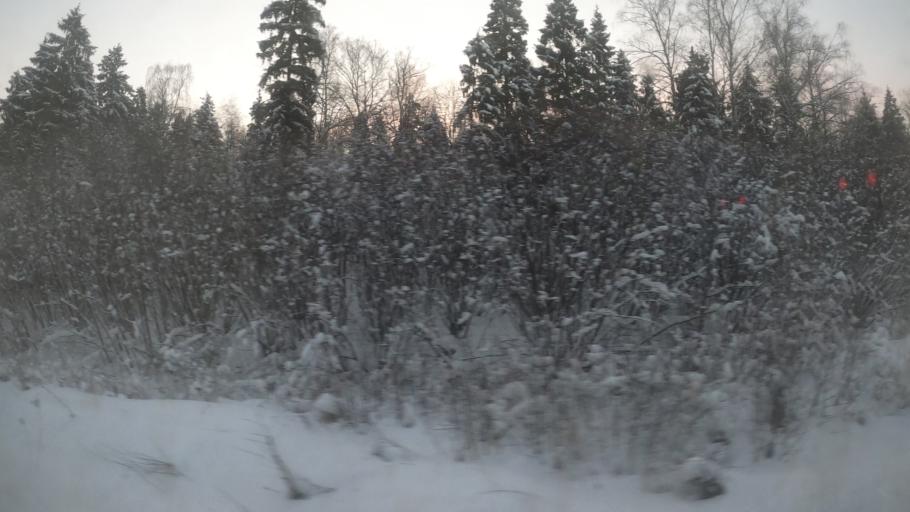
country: RU
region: Moskovskaya
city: Lugovaya
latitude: 56.0628
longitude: 37.4898
